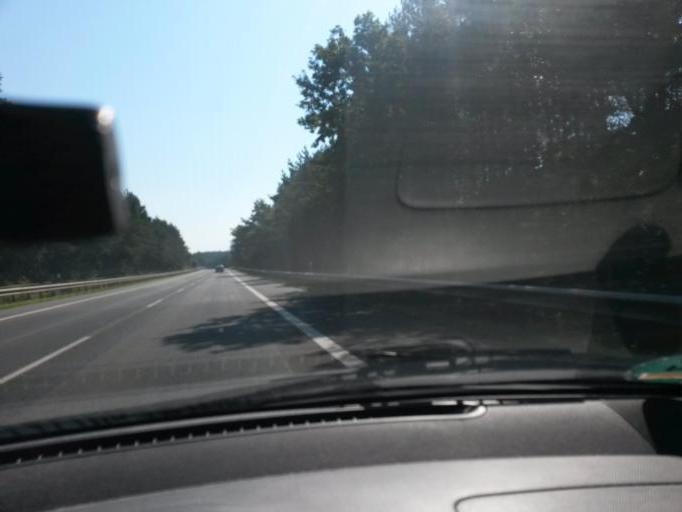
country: DE
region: Lower Saxony
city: Wendisch Evern
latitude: 53.2356
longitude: 10.4845
